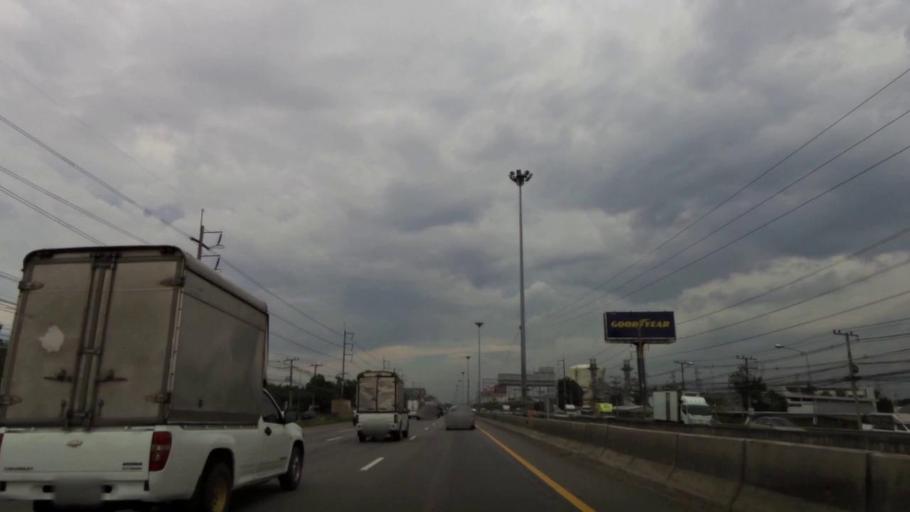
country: TH
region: Pathum Thani
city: Khlong Luang
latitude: 14.0247
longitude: 100.6158
